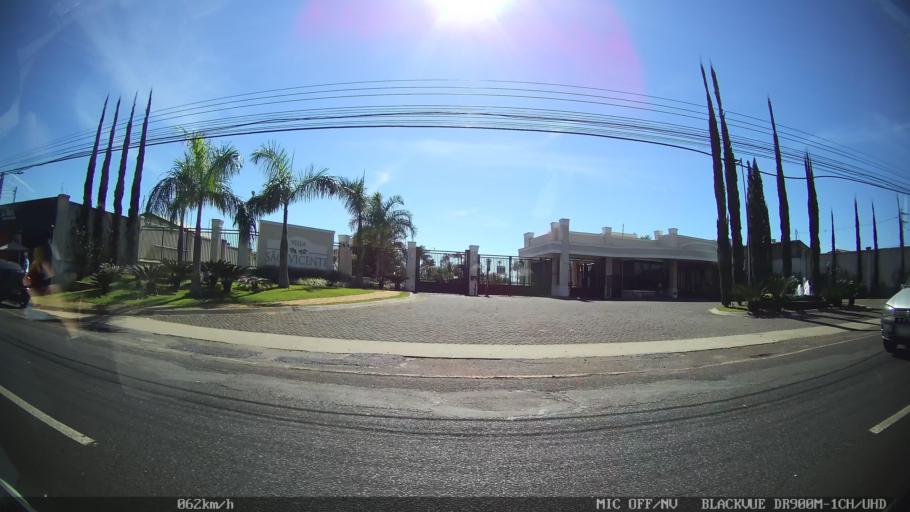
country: BR
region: Sao Paulo
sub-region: Franca
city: Franca
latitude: -20.5578
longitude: -47.3807
